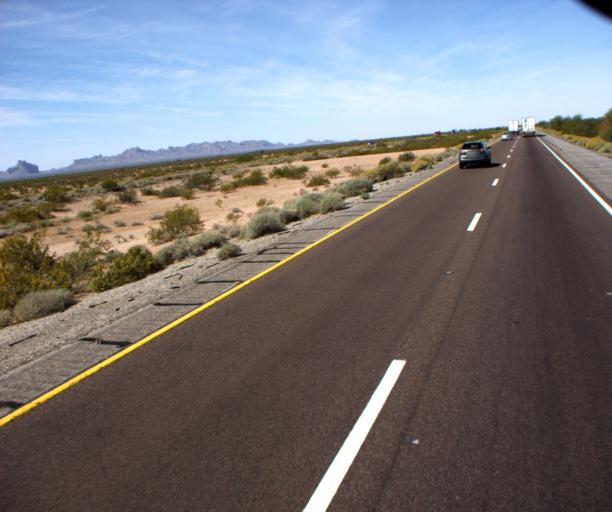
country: US
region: Arizona
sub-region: La Paz County
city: Salome
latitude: 33.5486
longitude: -113.2167
